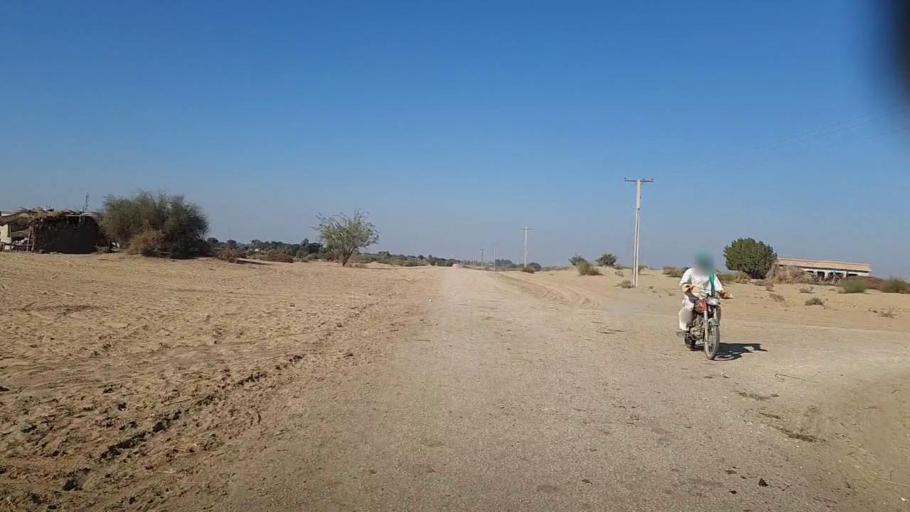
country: PK
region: Sindh
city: Khairpur
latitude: 27.9241
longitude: 69.7501
